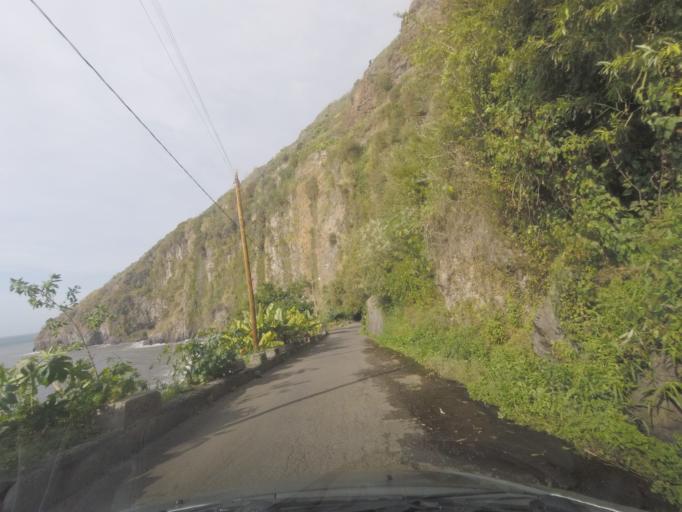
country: PT
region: Madeira
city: Ponta do Sol
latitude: 32.6901
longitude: -17.1196
